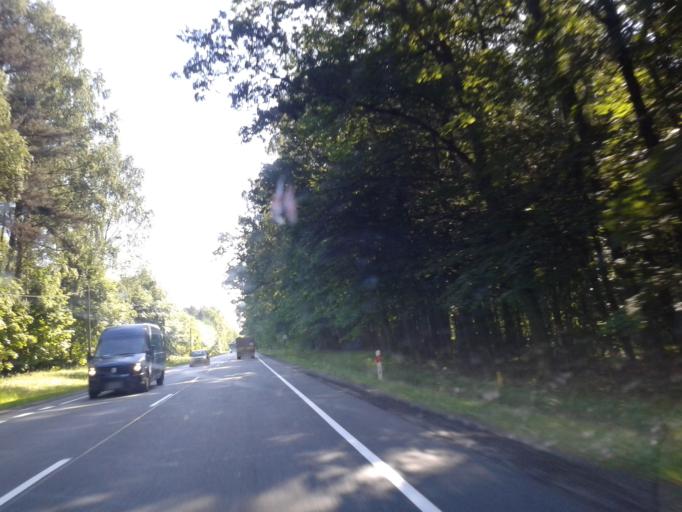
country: PL
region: Pomeranian Voivodeship
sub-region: Powiat chojnicki
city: Czersk
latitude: 53.7826
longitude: 17.9091
